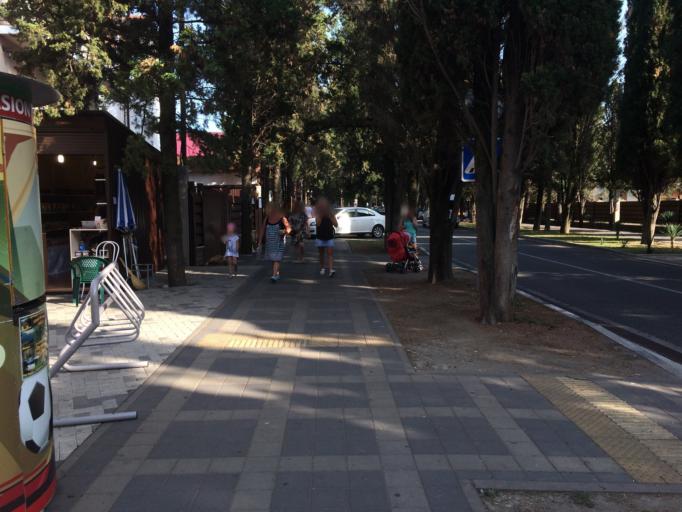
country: RU
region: Krasnodarskiy
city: Adler
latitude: 43.3917
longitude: 39.9830
